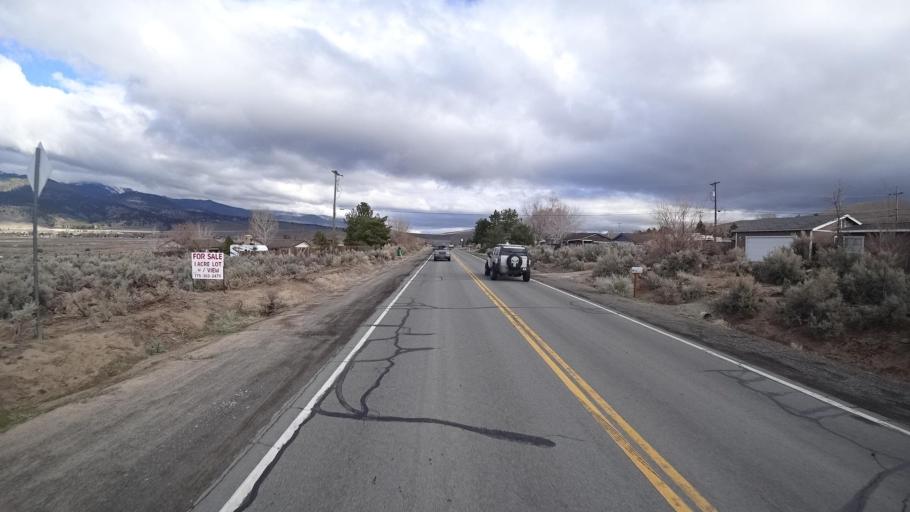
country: US
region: Nevada
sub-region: Storey County
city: Virginia City
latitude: 39.3095
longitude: -119.7885
